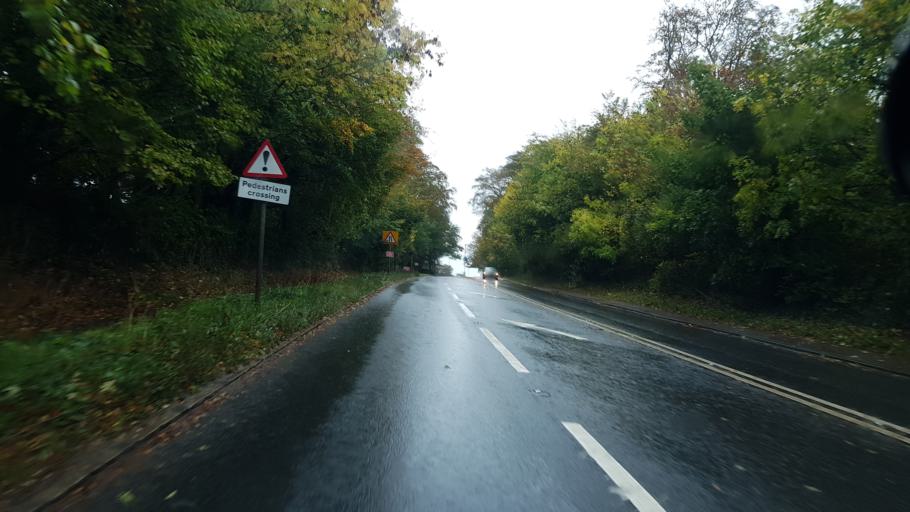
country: GB
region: England
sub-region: Gloucestershire
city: Stow on the Wold
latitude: 51.9240
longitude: -1.7257
